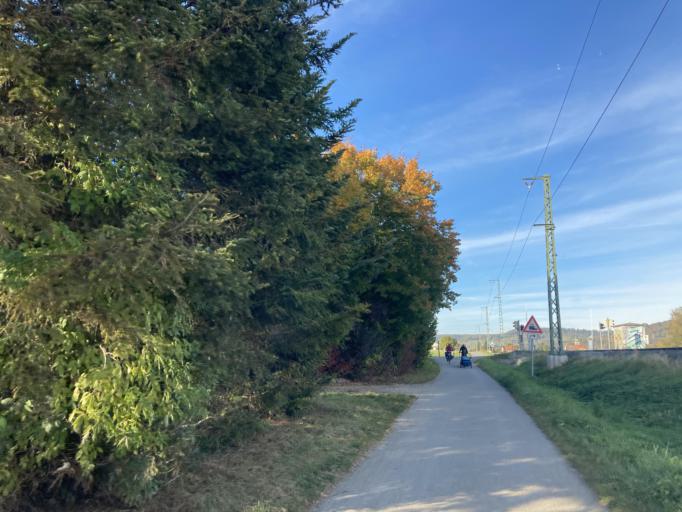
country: DE
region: Baden-Wuerttemberg
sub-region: Tuebingen Region
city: Rottenburg
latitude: 48.5436
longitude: 8.9636
